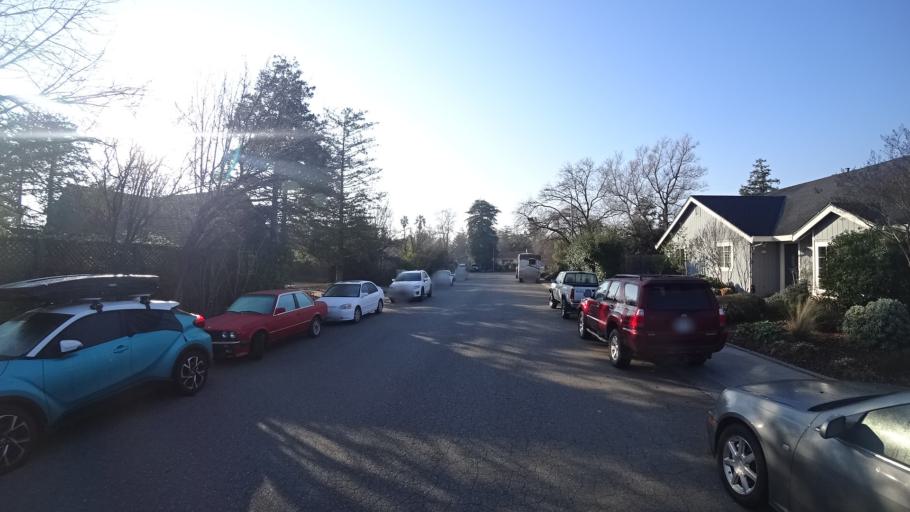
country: US
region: California
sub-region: Yolo County
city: Davis
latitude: 38.5570
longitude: -121.7850
